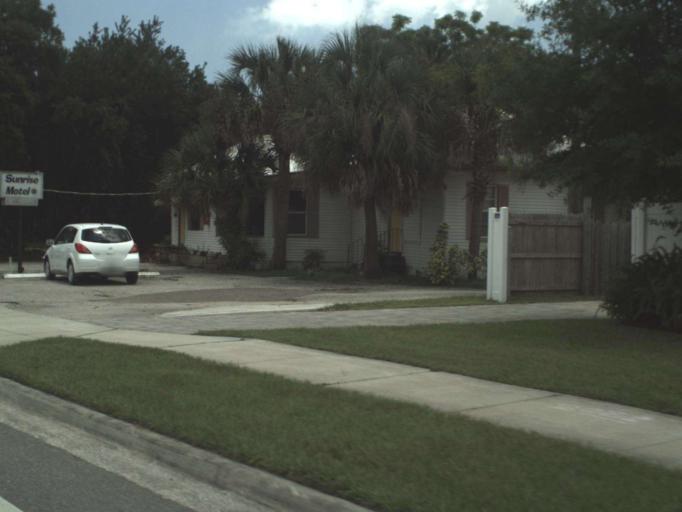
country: US
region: Florida
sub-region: Volusia County
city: New Smyrna Beach
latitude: 29.0193
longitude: -80.9352
